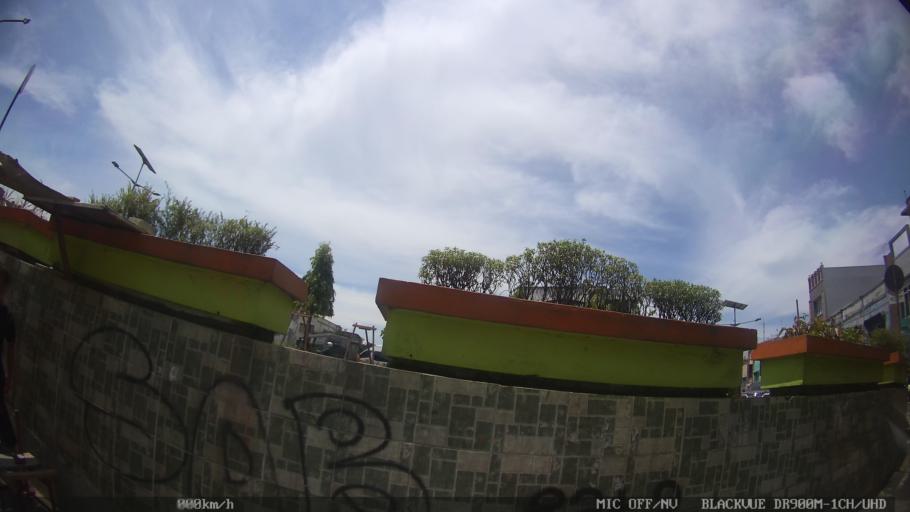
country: ID
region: North Sumatra
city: Binjai
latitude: 3.6109
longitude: 98.4922
